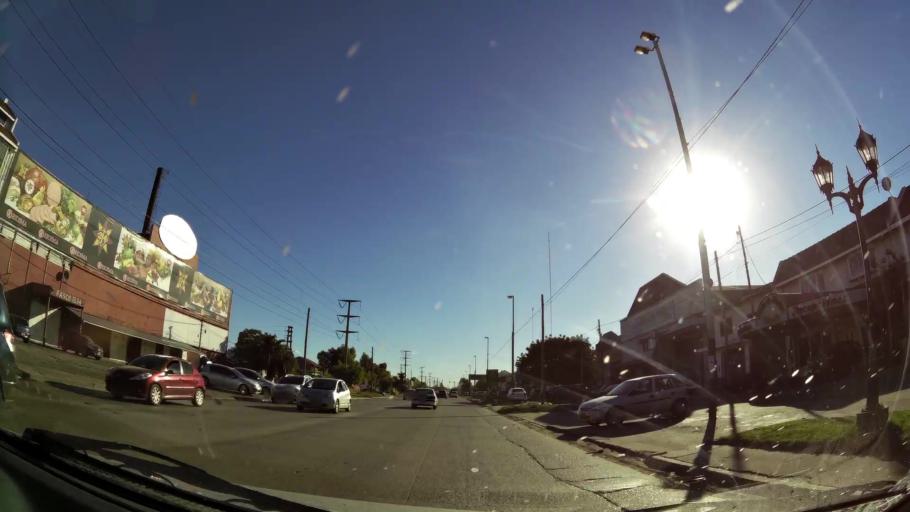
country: AR
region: Buenos Aires
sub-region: Partido de Quilmes
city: Quilmes
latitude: -34.7419
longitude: -58.3234
